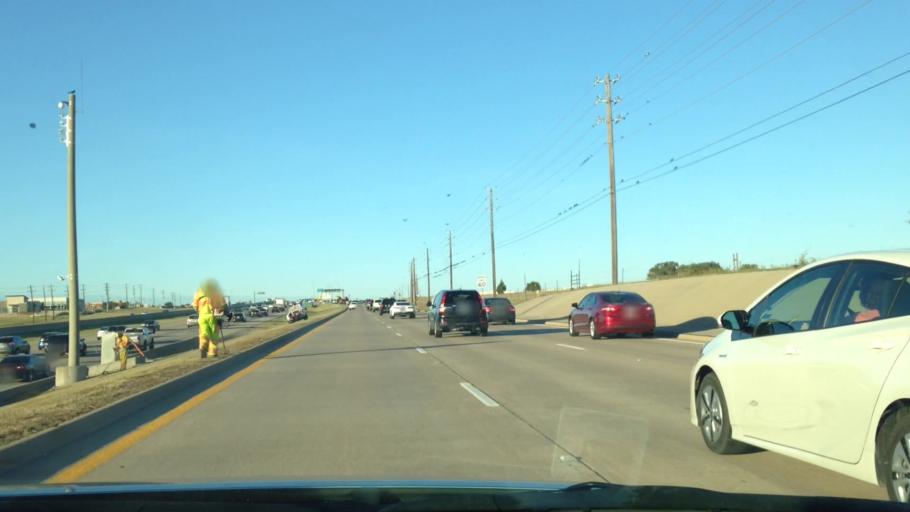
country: US
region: Texas
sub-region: Collin County
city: Frisco
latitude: 33.1165
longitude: -96.7587
